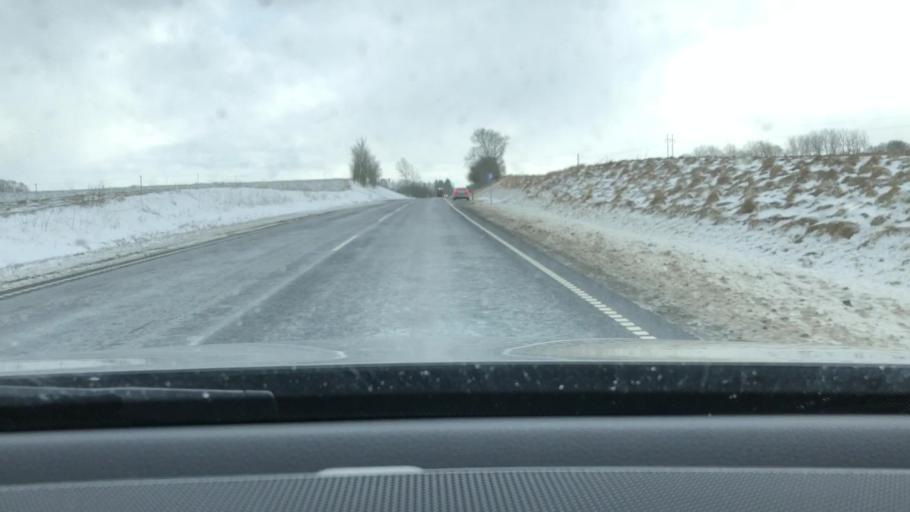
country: DK
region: Central Jutland
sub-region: Favrskov Kommune
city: Hammel
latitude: 56.1968
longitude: 9.8492
